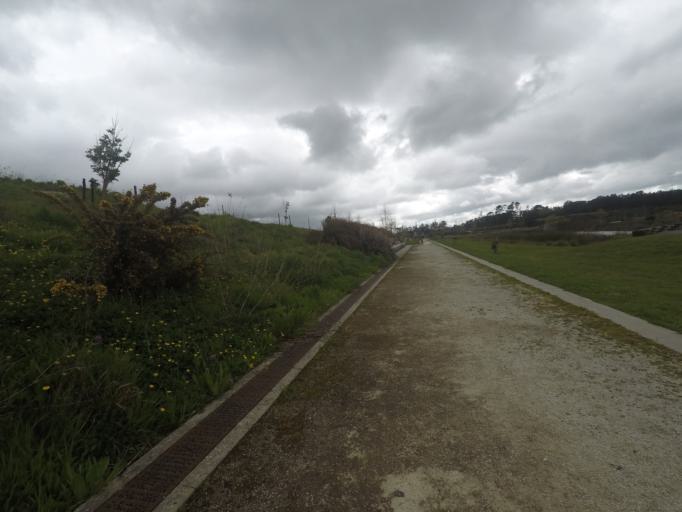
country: NZ
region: Auckland
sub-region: Auckland
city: Rosebank
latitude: -36.8130
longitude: 174.6056
